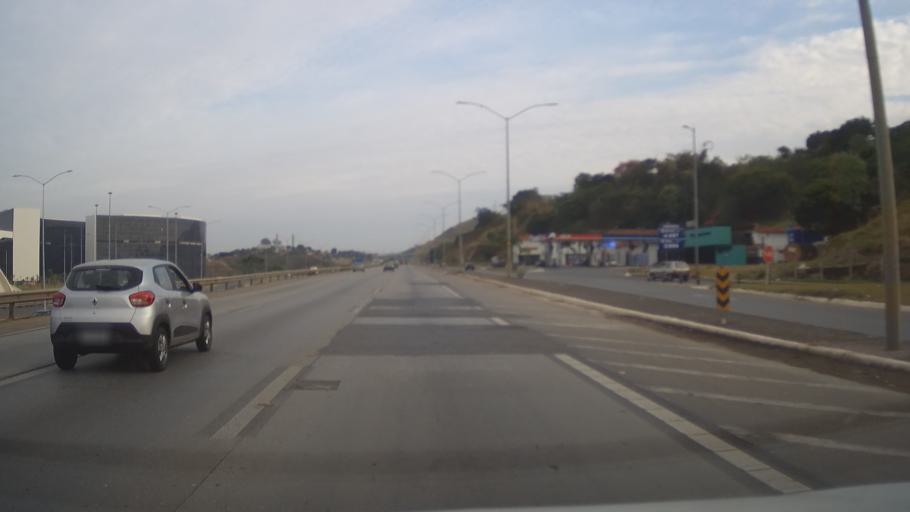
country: BR
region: Minas Gerais
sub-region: Santa Luzia
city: Santa Luzia
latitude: -19.7898
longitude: -43.9489
